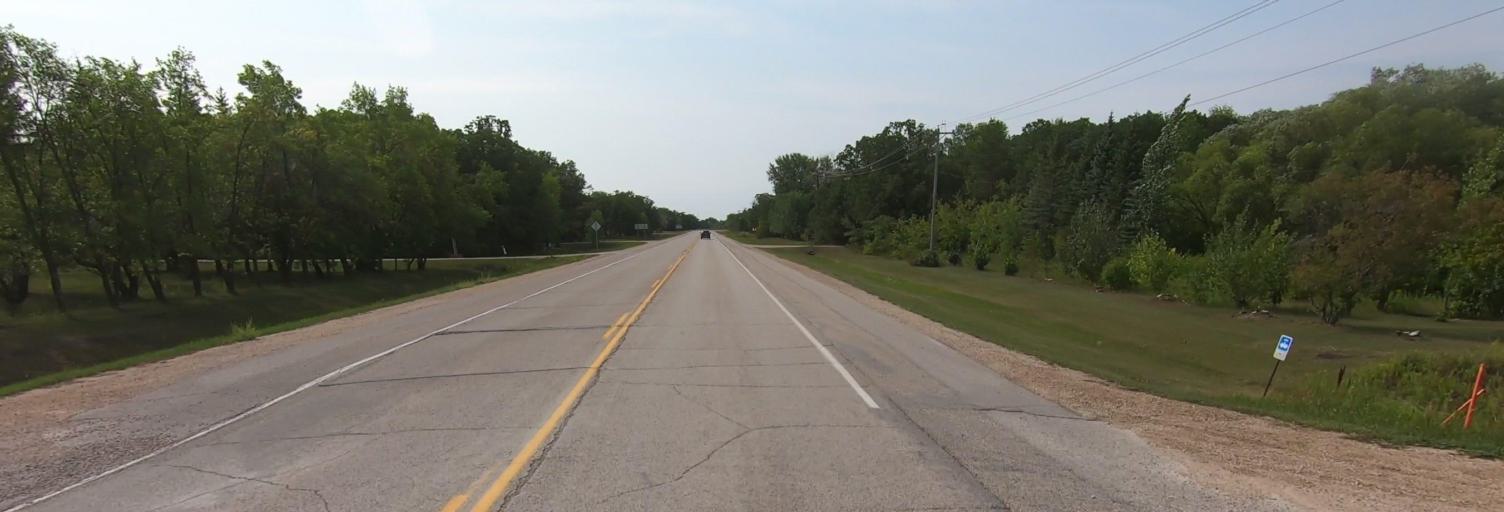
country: CA
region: Manitoba
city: Niverville
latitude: 49.7090
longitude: -97.0908
